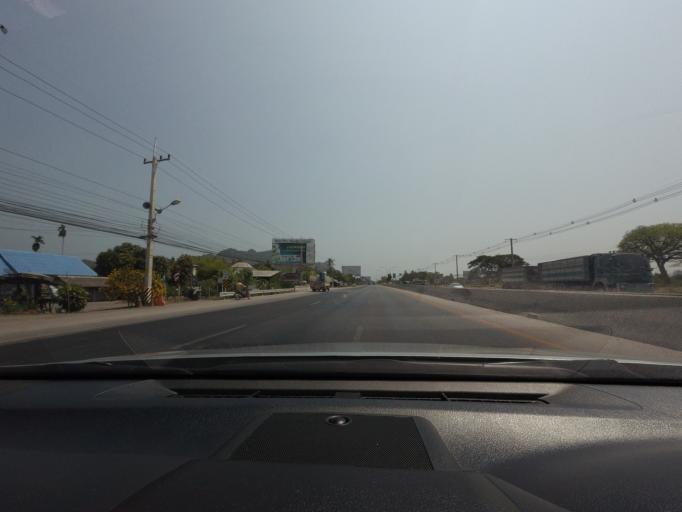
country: TH
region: Phetchaburi
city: Cha-am
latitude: 12.8475
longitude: 99.9275
